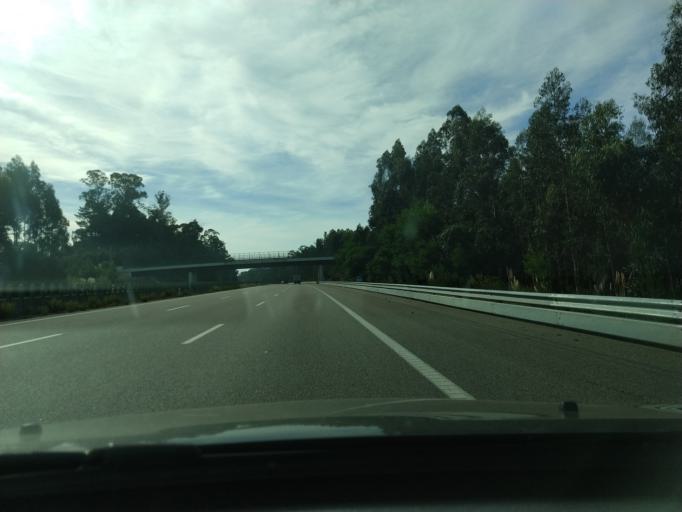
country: PT
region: Aveiro
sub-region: Ovar
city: Valega
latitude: 40.8697
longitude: -8.5600
